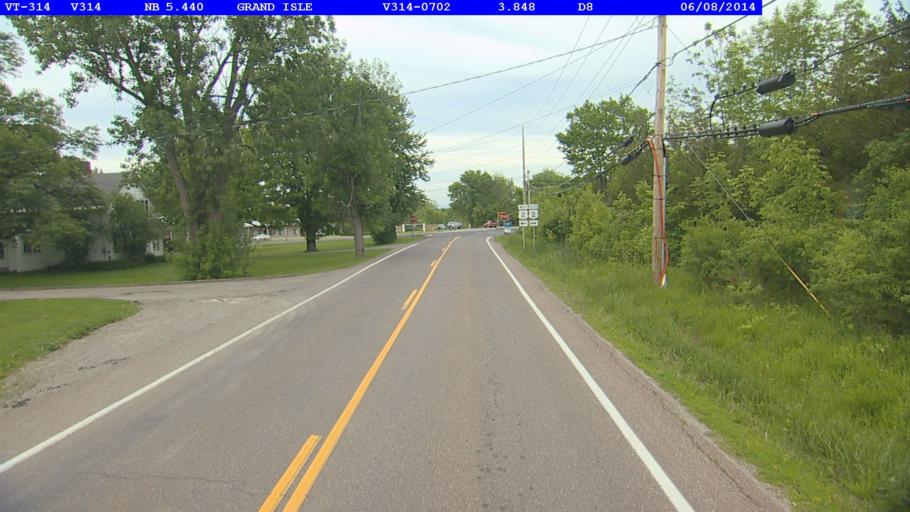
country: US
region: New York
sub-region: Clinton County
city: Cumberland Head
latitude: 44.7032
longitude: -73.3037
